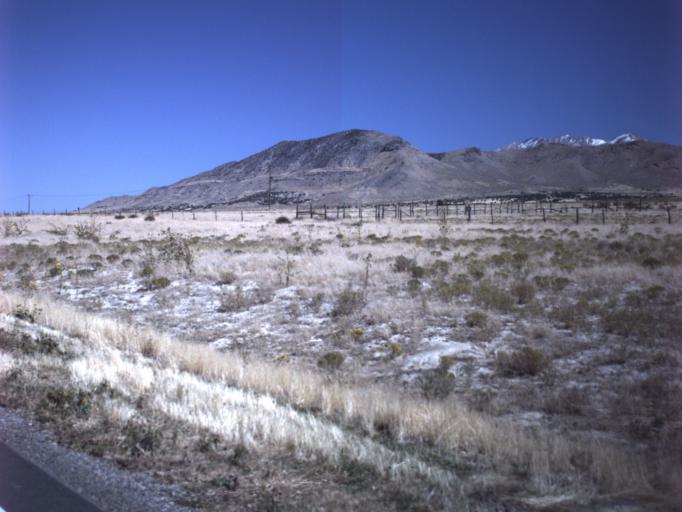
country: US
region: Utah
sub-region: Tooele County
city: Grantsville
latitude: 40.5136
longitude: -112.7477
